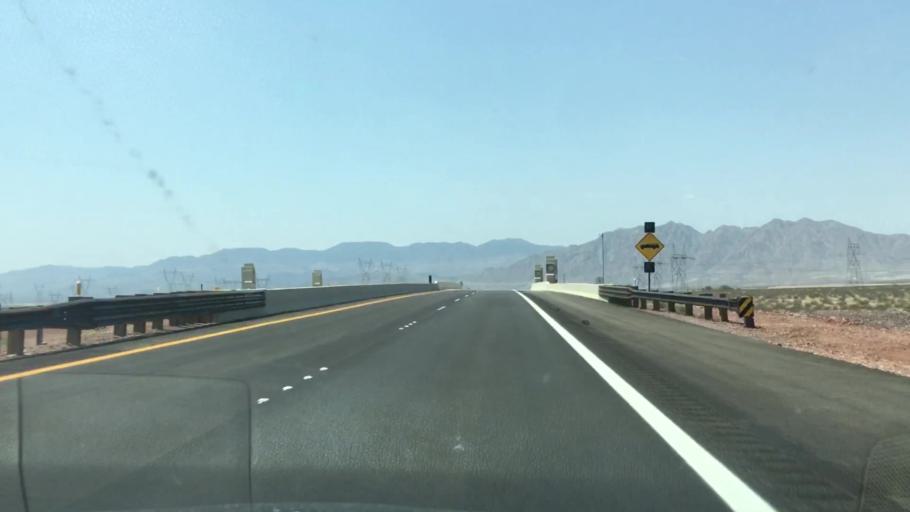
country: US
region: Nevada
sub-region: Clark County
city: Boulder City
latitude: 35.9344
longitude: -114.8400
